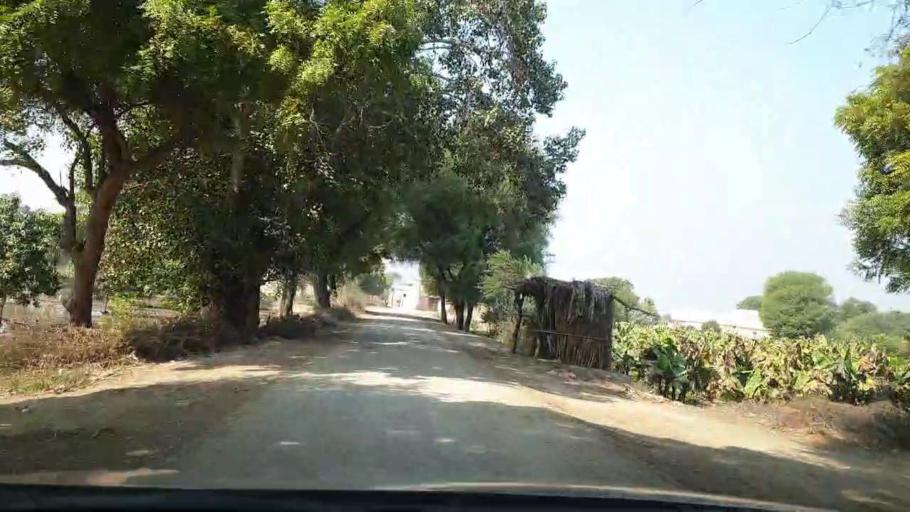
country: PK
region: Sindh
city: Tando Allahyar
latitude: 25.5315
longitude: 68.7696
